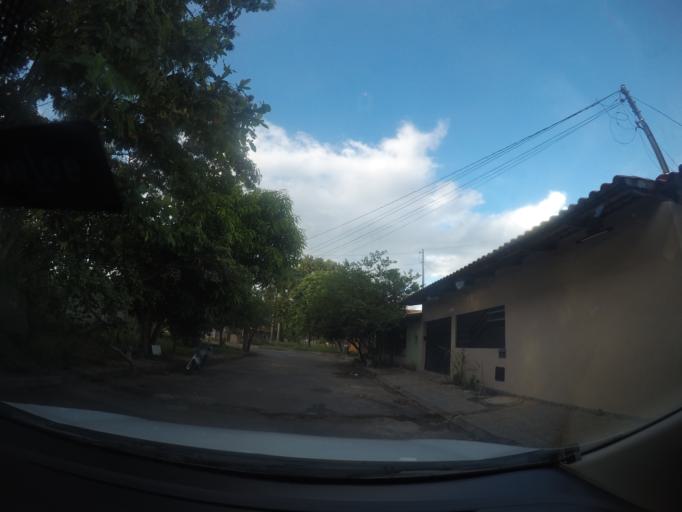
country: BR
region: Goias
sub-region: Goiania
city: Goiania
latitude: -16.6837
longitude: -49.3158
